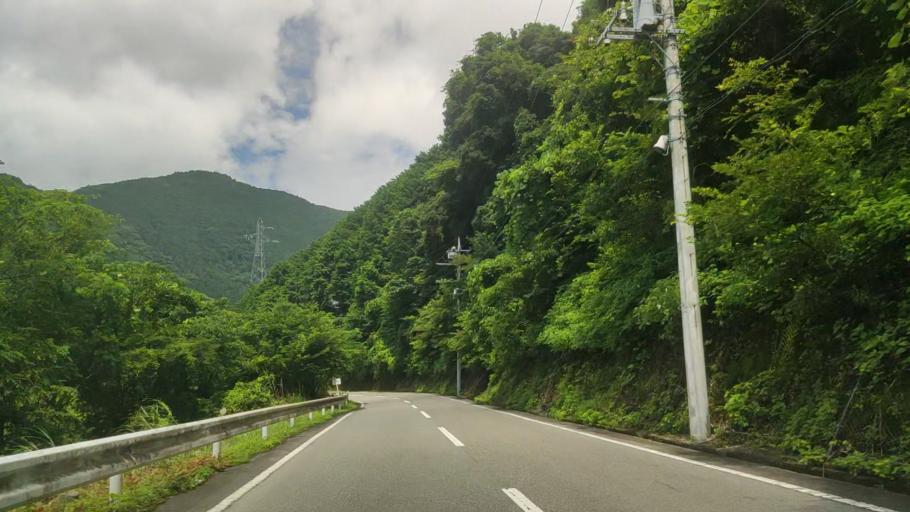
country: JP
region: Shizuoka
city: Fujinomiya
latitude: 35.2416
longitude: 138.5099
